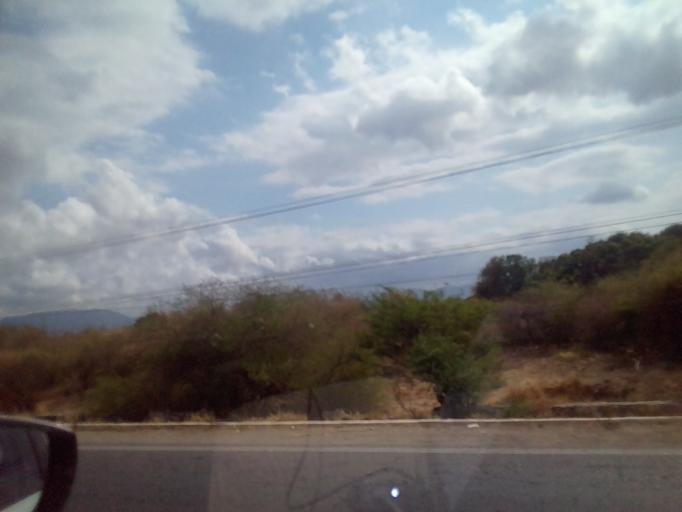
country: MX
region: Oaxaca
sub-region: Santo Domingo Tehuantepec
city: Santo Domingo Tehuantepec
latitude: 16.3036
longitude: -95.2340
